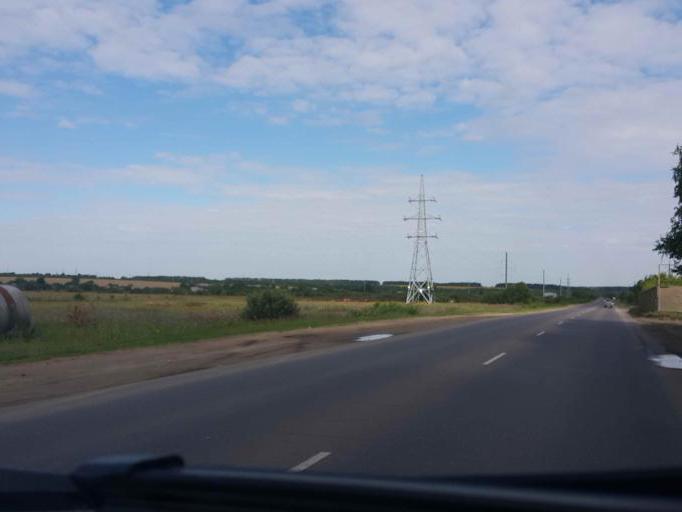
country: RU
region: Tambov
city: Bokino
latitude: 52.6423
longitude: 41.4253
